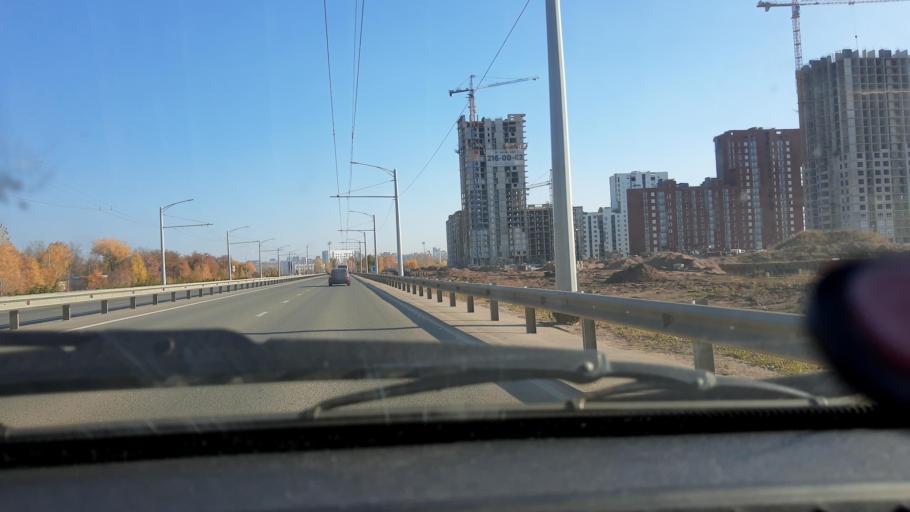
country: RU
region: Bashkortostan
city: Mikhaylovka
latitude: 54.7736
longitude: 55.8982
